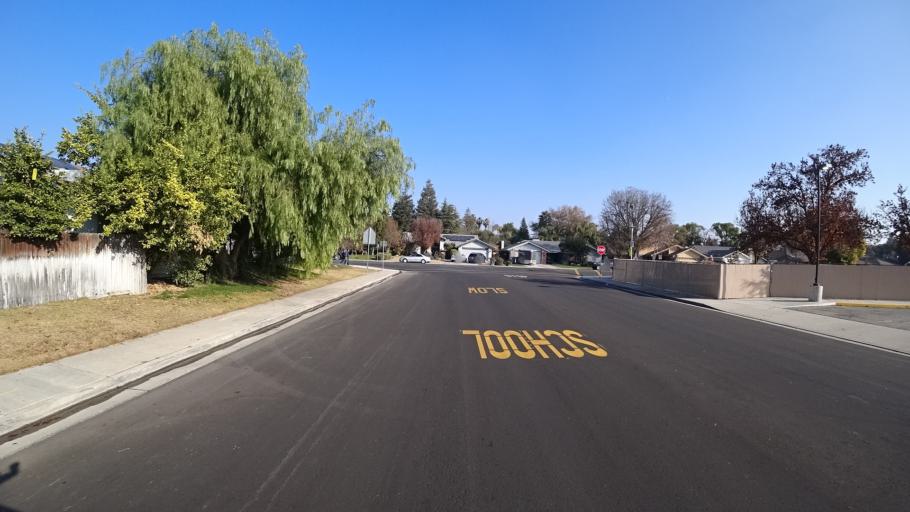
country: US
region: California
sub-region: Kern County
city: Greenacres
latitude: 35.3303
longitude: -119.1066
